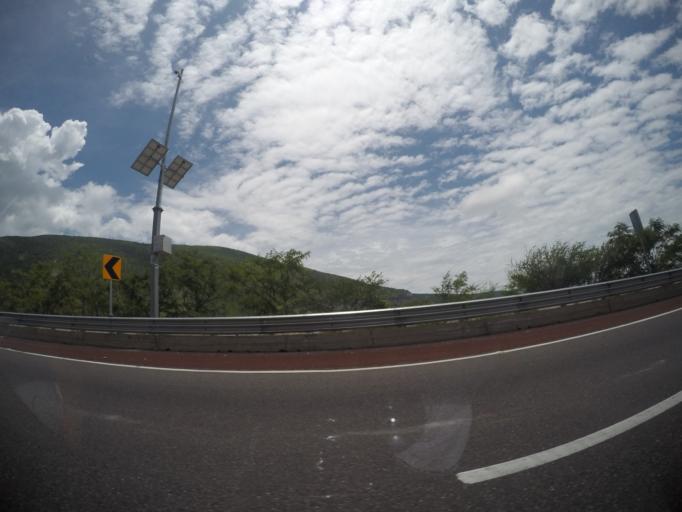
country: MX
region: Guerrero
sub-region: Eduardo Neri
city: Tlanipatla
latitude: 17.8533
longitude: -99.4068
